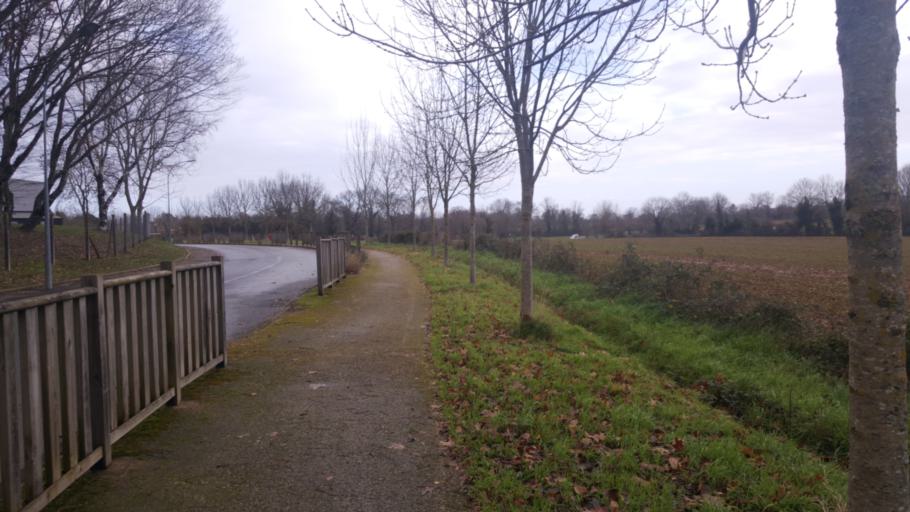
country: FR
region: Poitou-Charentes
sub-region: Departement des Deux-Sevres
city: Melle
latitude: 46.2288
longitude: -0.1334
